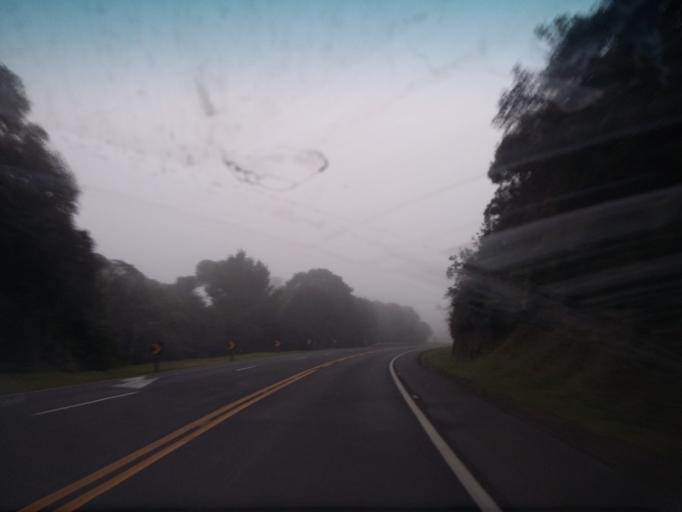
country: BR
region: Santa Catarina
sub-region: Correia Pinto
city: Correia Pinto
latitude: -27.4173
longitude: -50.4148
